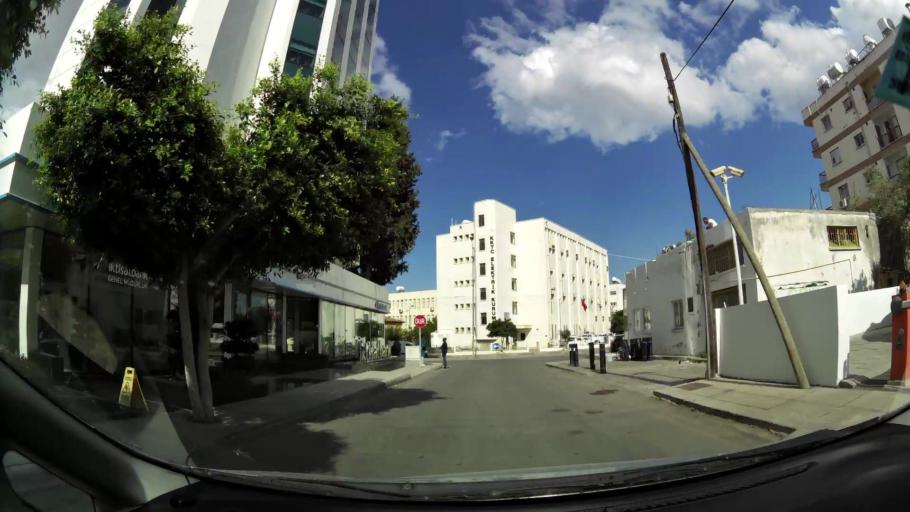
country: CY
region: Lefkosia
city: Nicosia
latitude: 35.1932
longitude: 33.3487
